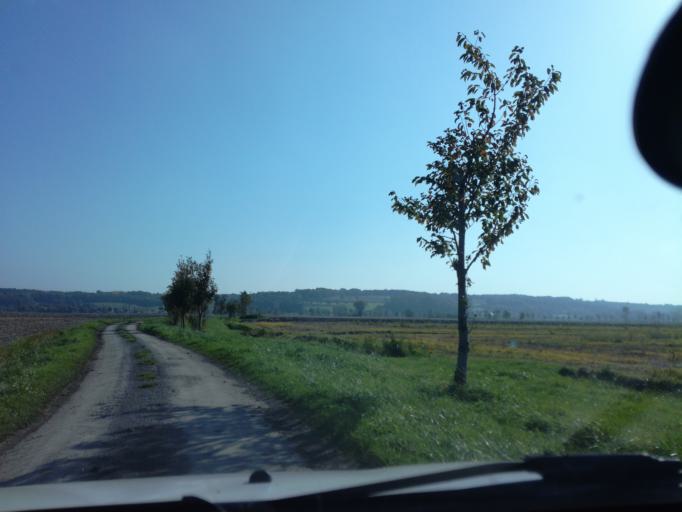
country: FR
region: Brittany
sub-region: Departement d'Ille-et-Vilaine
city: Cherrueix
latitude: 48.5889
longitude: -1.6886
